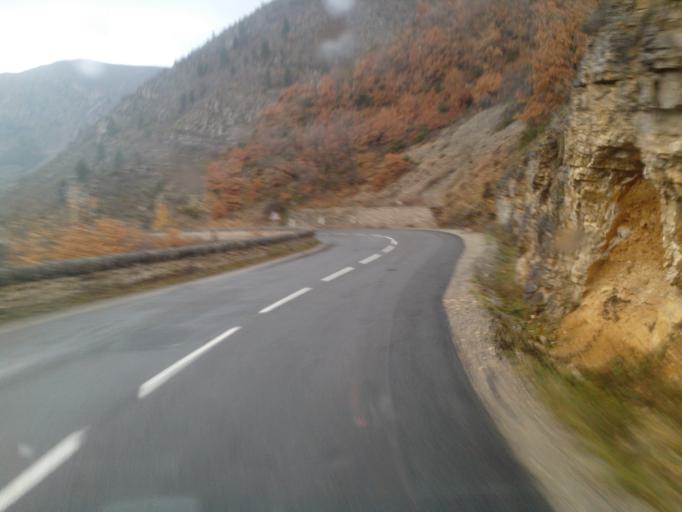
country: FR
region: Languedoc-Roussillon
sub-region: Departement de la Lozere
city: Florac
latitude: 44.3456
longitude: 3.4654
